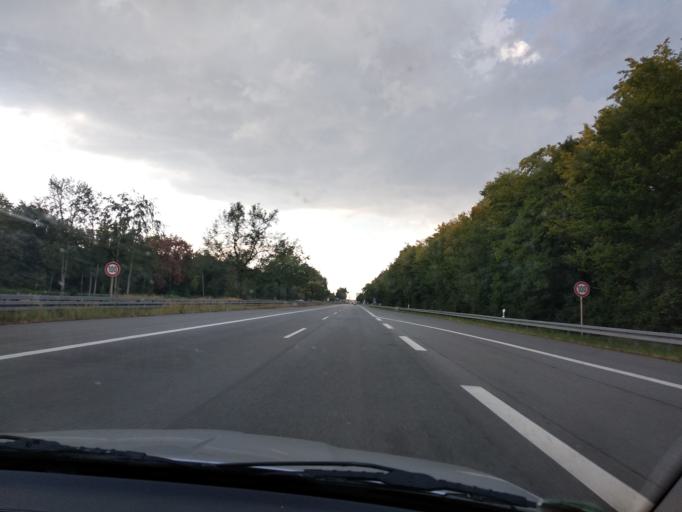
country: DE
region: Bavaria
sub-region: Upper Bavaria
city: Unterhaching
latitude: 48.0875
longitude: 11.5929
